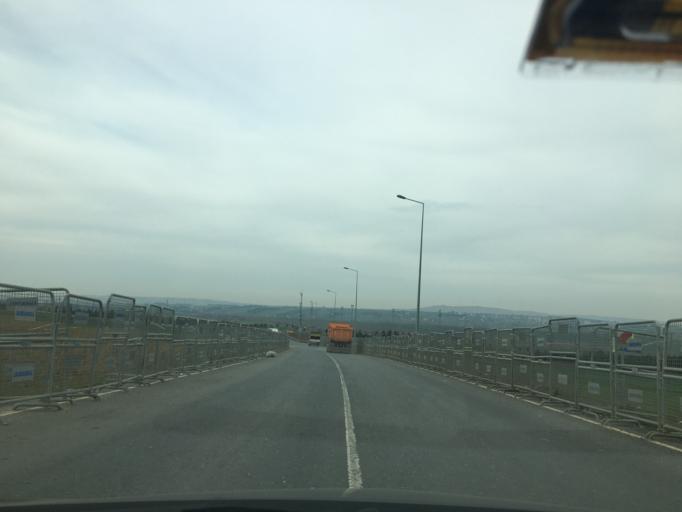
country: TR
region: Istanbul
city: Canta
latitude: 41.0962
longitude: 28.1537
